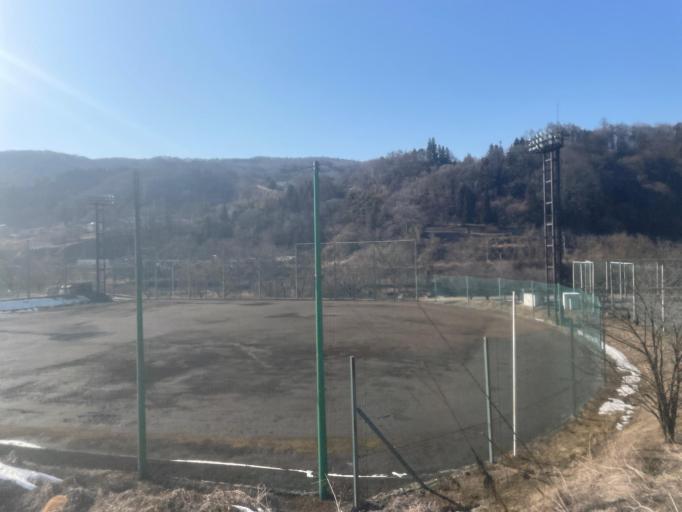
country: JP
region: Nagano
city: Komoro
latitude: 36.5390
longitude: 138.5598
